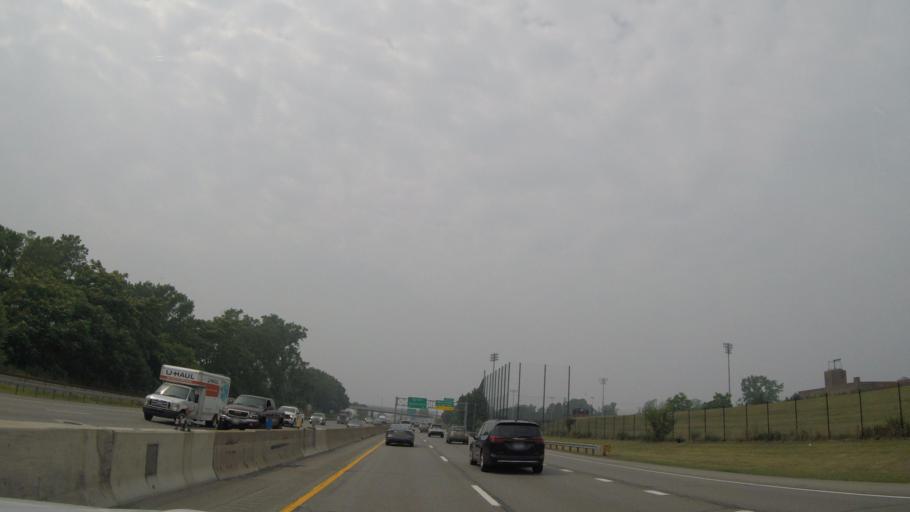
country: US
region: New York
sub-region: Erie County
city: Buffalo
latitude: 42.8958
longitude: -78.8953
